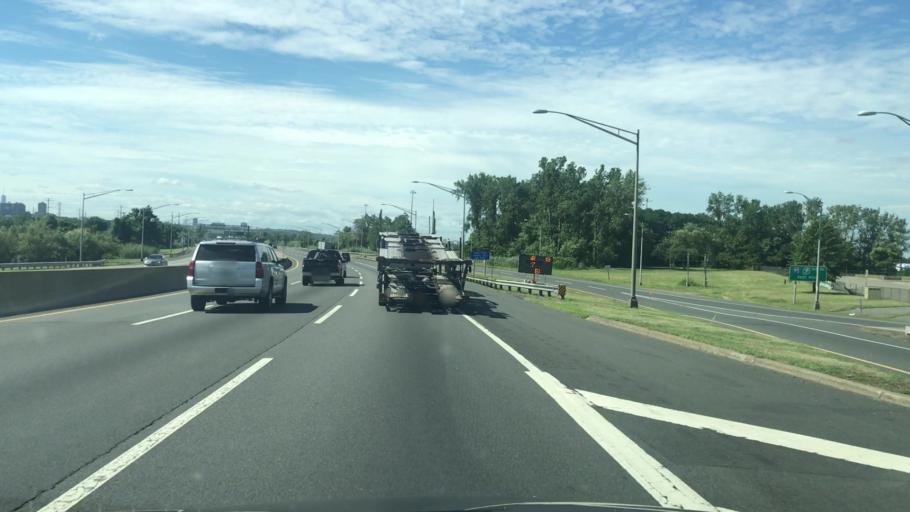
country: US
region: New Jersey
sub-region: Bergen County
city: Ridgefield
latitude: 40.8266
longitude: -74.0267
